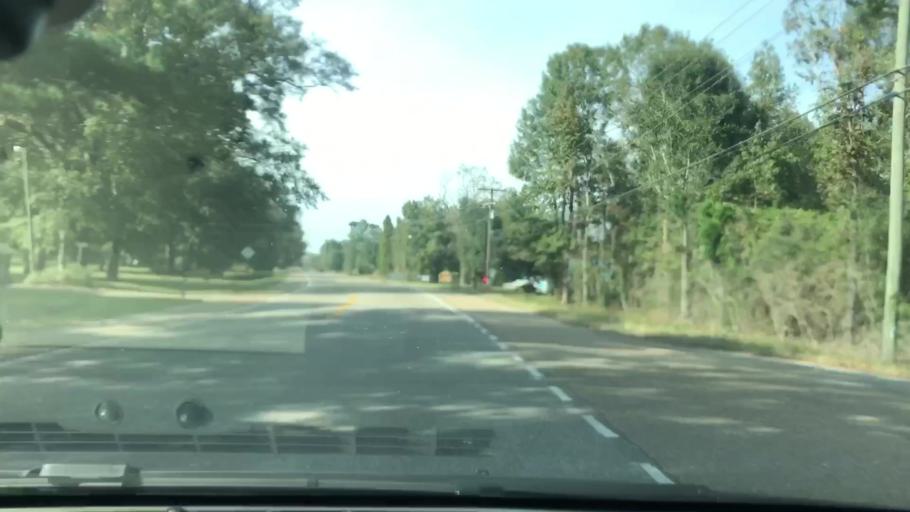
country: US
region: Louisiana
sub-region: Saint Tammany Parish
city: Pearl River
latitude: 30.4036
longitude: -89.7660
